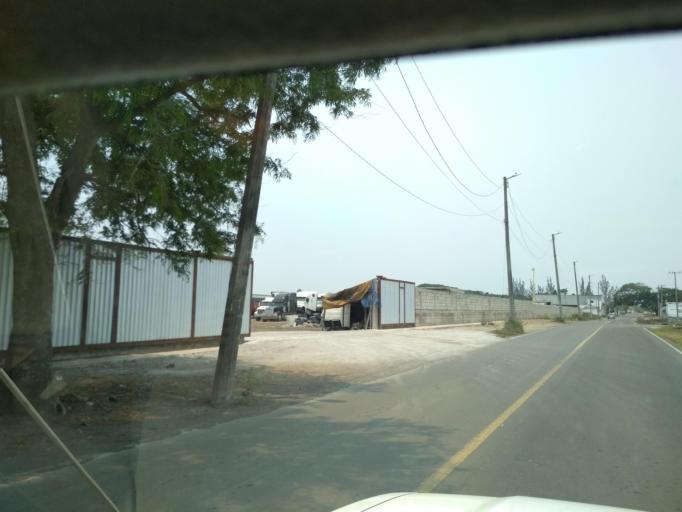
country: MX
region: Veracruz
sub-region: Veracruz
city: Delfino Victoria (Santa Fe)
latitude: 19.2085
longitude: -96.2653
